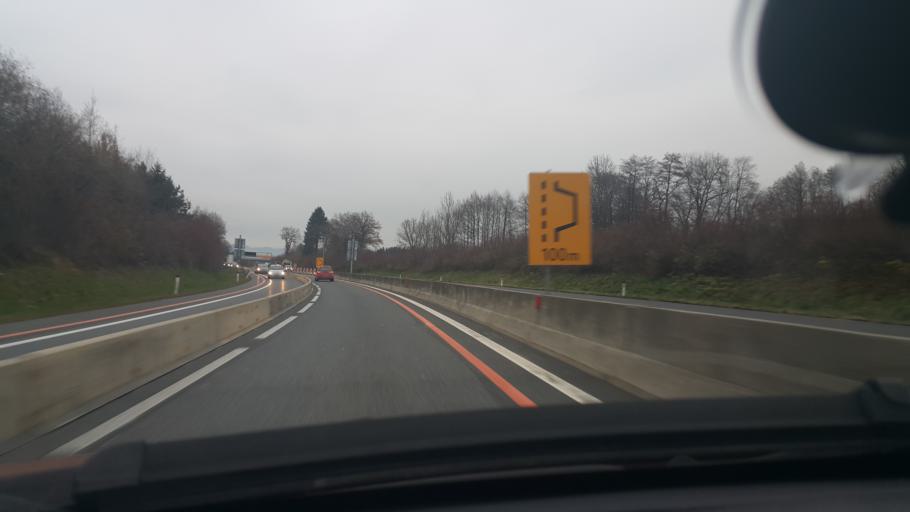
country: AT
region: Carinthia
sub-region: Klagenfurt am Woerthersee
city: Klagenfurt am Woerthersee
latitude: 46.6502
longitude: 14.2613
